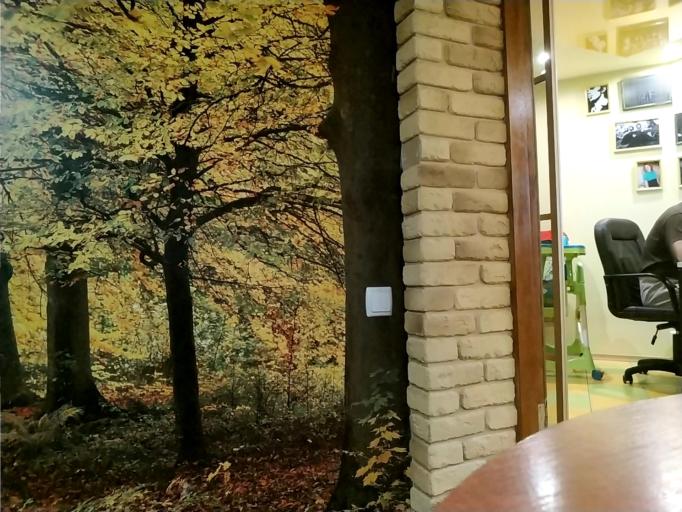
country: RU
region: Tverskaya
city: Staraya Toropa
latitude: 56.3387
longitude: 31.8589
